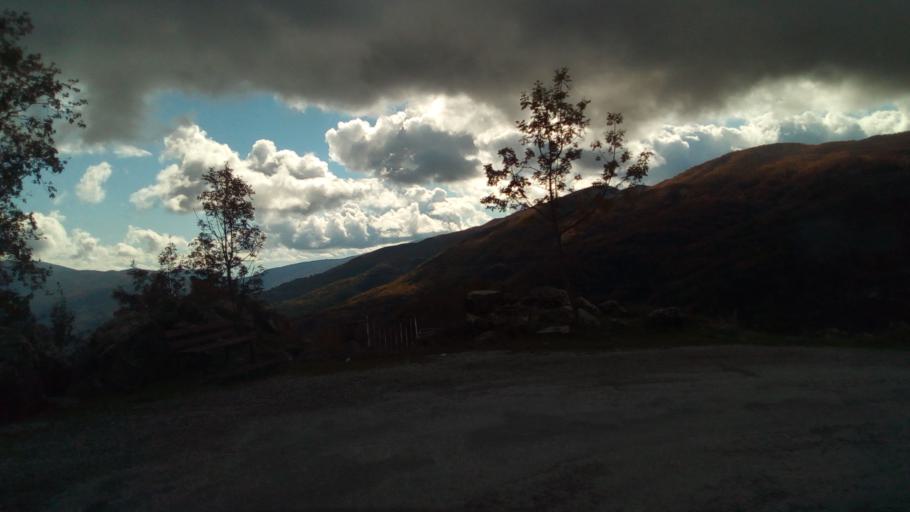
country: GR
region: Central Greece
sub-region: Nomos Fokidos
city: Lidoriki
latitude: 38.5650
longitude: 21.9815
